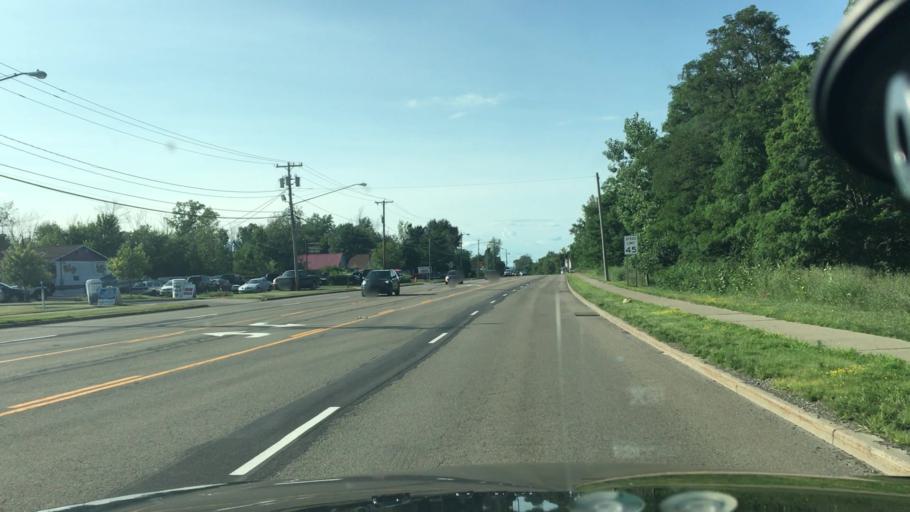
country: US
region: New York
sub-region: Erie County
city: Wanakah
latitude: 42.7588
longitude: -78.8612
